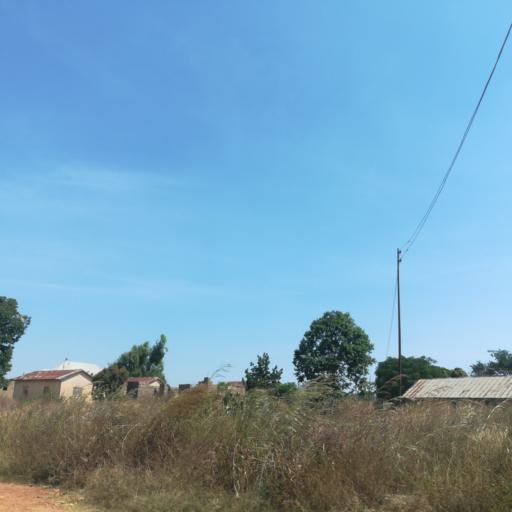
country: NG
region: Plateau
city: Jos
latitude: 9.8565
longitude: 8.9301
